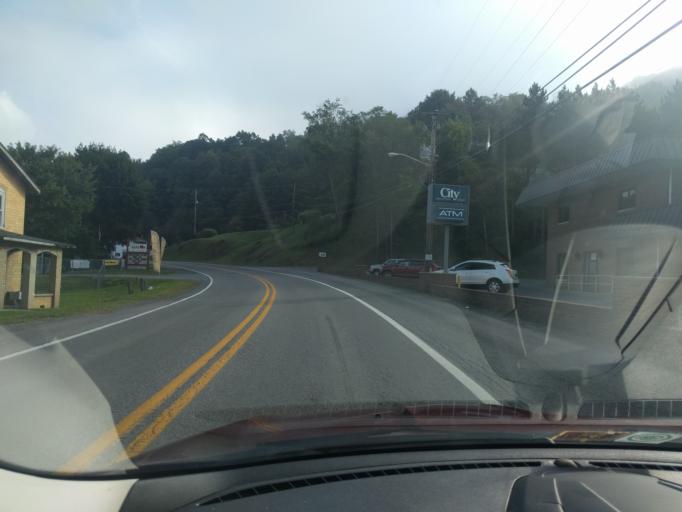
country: US
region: West Virginia
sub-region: Greenbrier County
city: Rainelle
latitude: 37.9737
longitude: -80.7587
